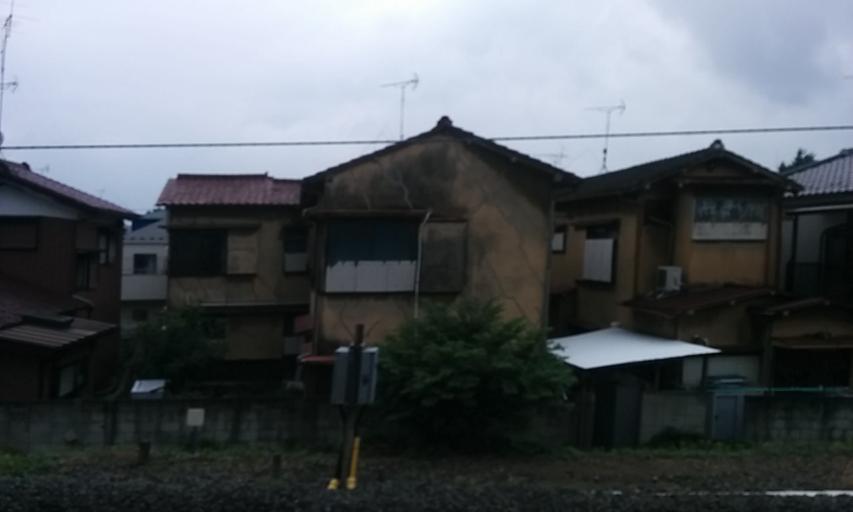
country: JP
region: Chiba
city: Matsudo
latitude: 35.7783
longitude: 139.8985
